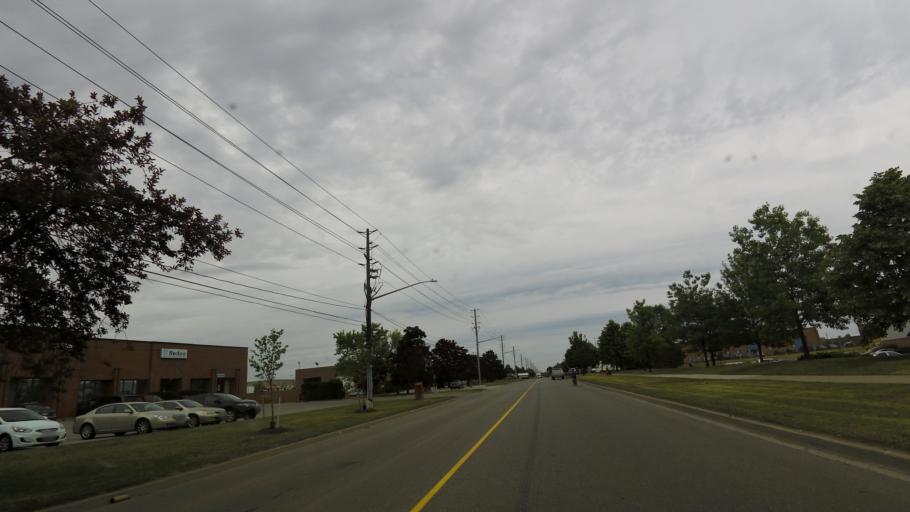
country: CA
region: Ontario
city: Oakville
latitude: 43.4149
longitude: -79.7290
